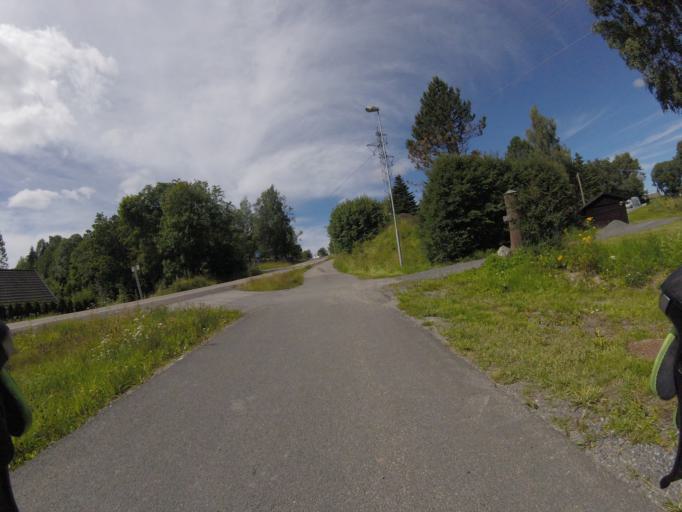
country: NO
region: Akershus
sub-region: Skedsmo
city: Lillestrom
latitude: 59.9459
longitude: 11.0256
